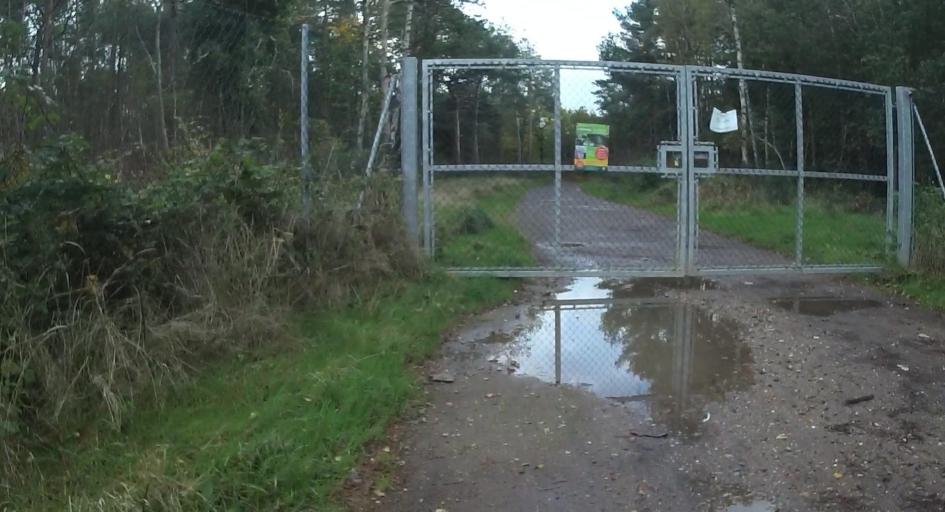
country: GB
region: England
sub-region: Surrey
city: Pirbright
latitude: 51.3108
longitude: -0.6910
